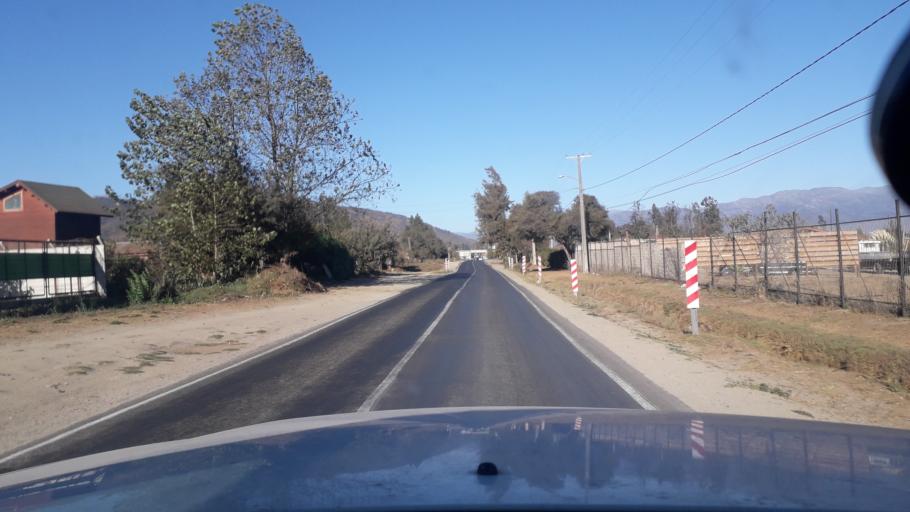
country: CL
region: Valparaiso
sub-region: Provincia de Marga Marga
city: Limache
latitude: -32.9697
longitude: -71.3068
